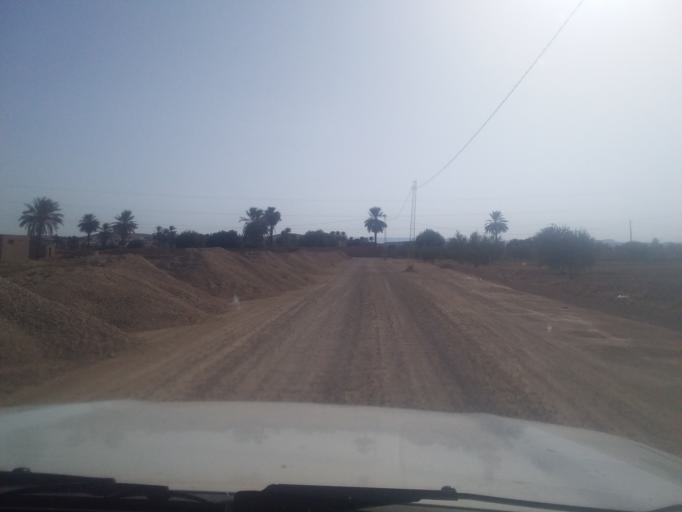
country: TN
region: Qabis
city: Matmata
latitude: 33.5903
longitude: 10.2682
